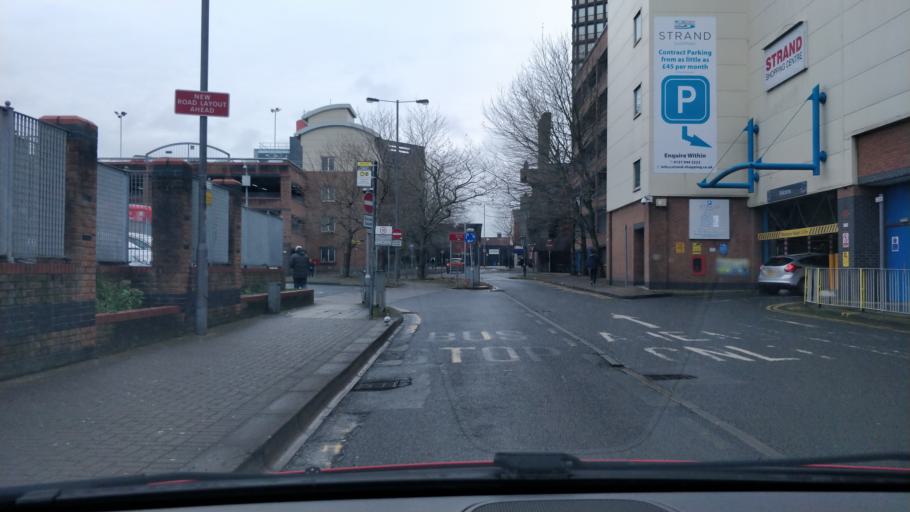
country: GB
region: England
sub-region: Sefton
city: Litherland
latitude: 53.4530
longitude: -2.9931
